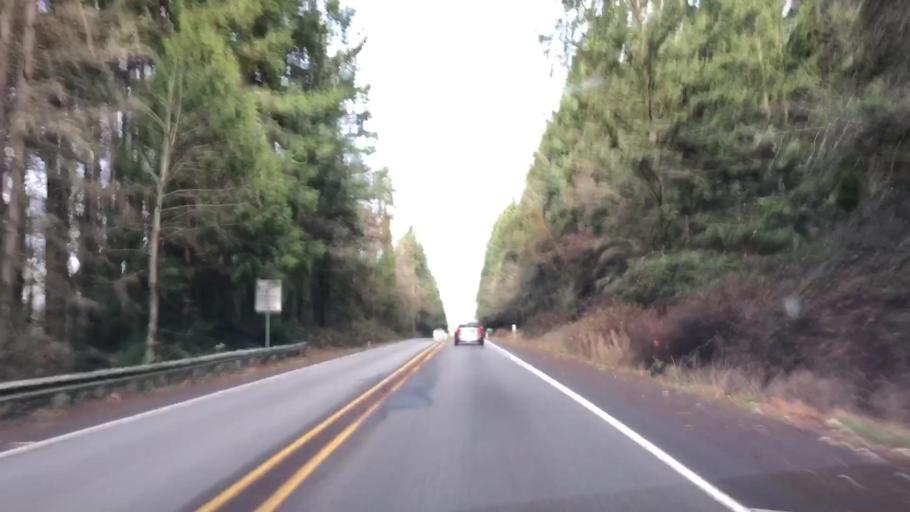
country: US
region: Washington
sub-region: Kitsap County
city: Bainbridge Island
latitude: 47.6752
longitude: -122.5348
